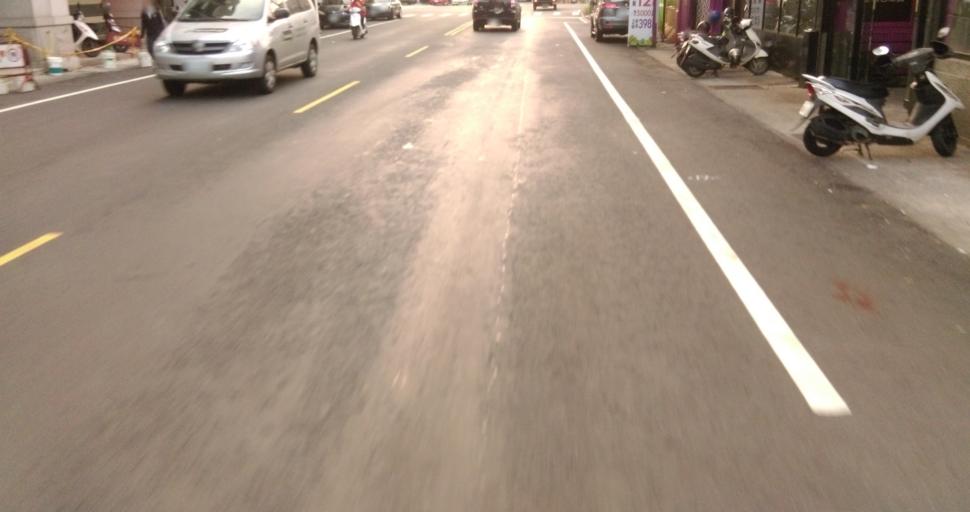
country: TW
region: Taiwan
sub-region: Hsinchu
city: Hsinchu
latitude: 24.8421
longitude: 120.9348
